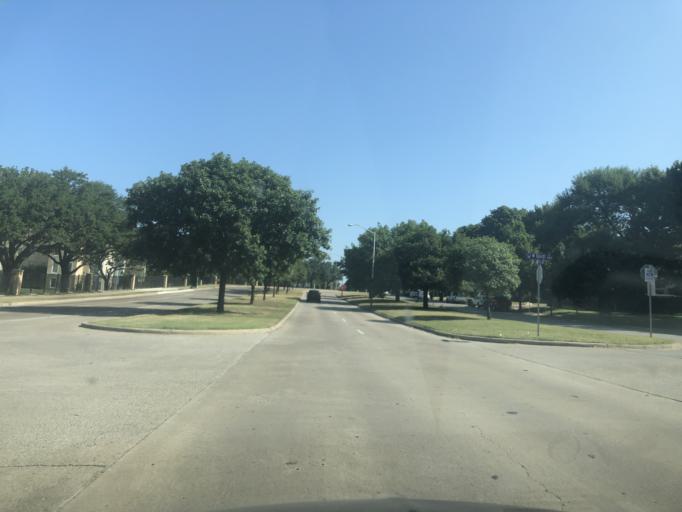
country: US
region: Texas
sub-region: Tarrant County
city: Fort Worth
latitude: 32.7039
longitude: -97.3652
